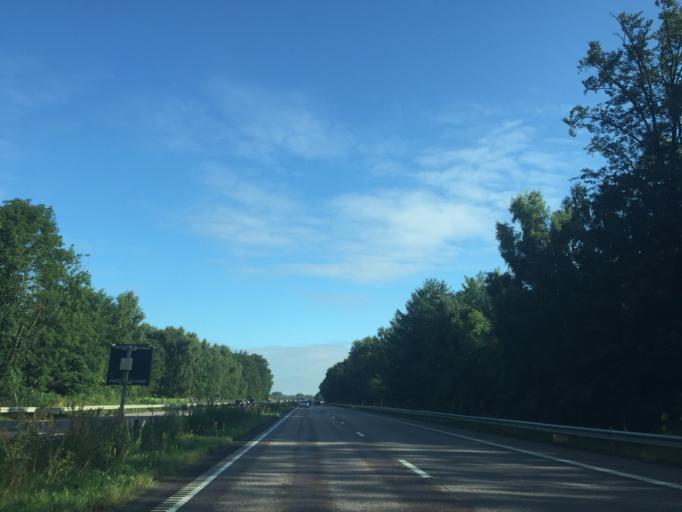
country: SE
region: Skane
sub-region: Helsingborg
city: Odakra
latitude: 56.0579
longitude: 12.7832
